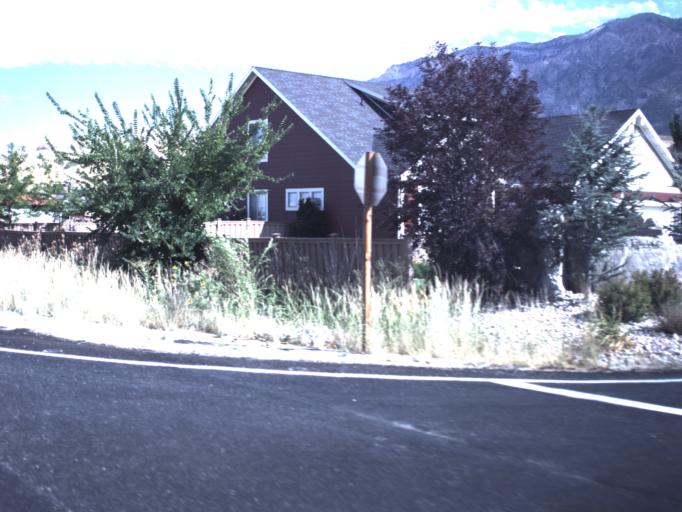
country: US
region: Utah
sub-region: Weber County
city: Pleasant View
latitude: 41.3182
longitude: -112.0144
